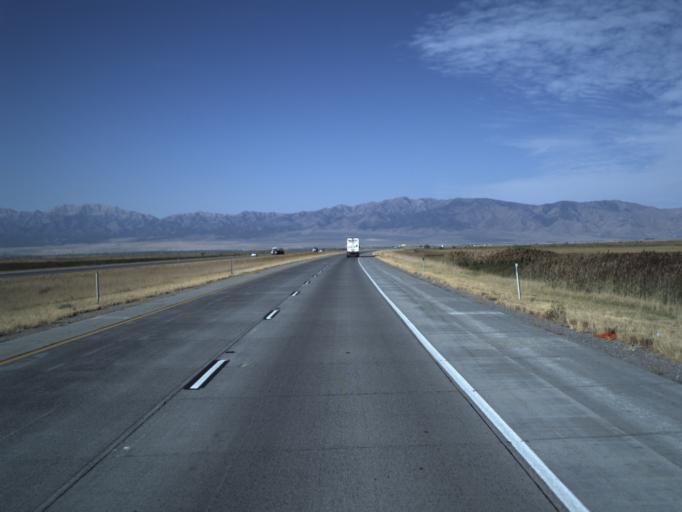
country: US
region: Utah
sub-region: Tooele County
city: Stansbury park
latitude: 40.6660
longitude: -112.3116
